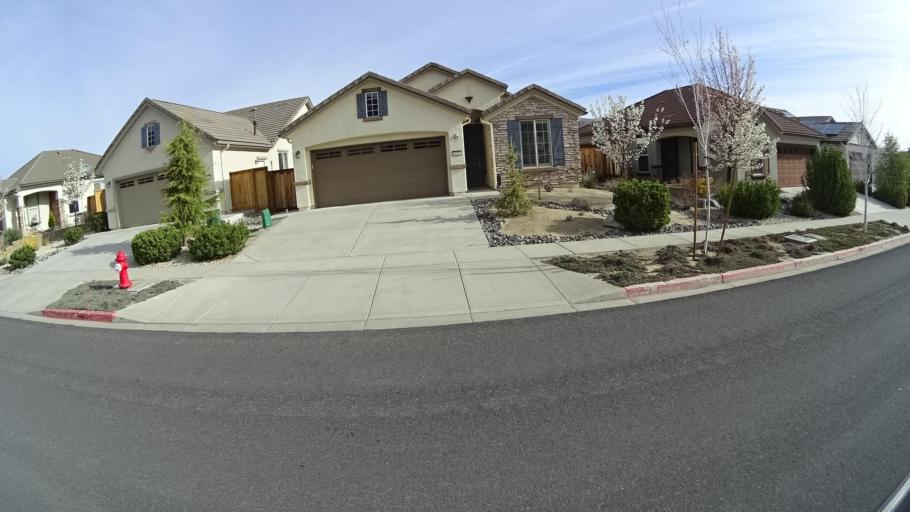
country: US
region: Nevada
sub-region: Washoe County
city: Mogul
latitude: 39.5207
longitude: -119.9519
